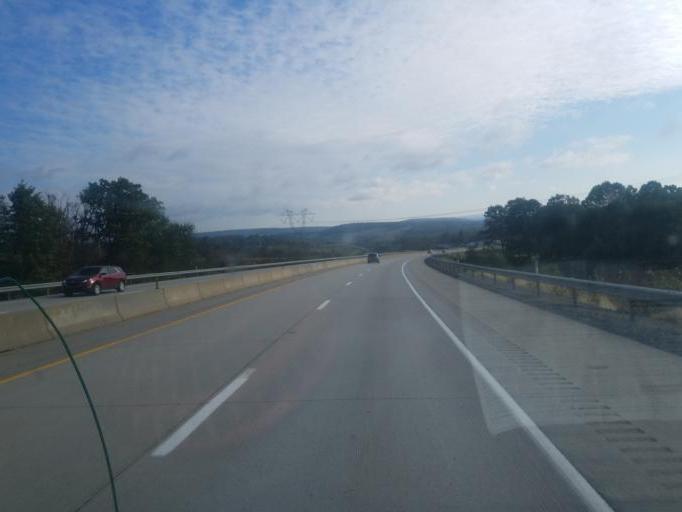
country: US
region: Pennsylvania
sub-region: Indiana County
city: Homer City
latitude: 40.4496
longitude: -79.0643
